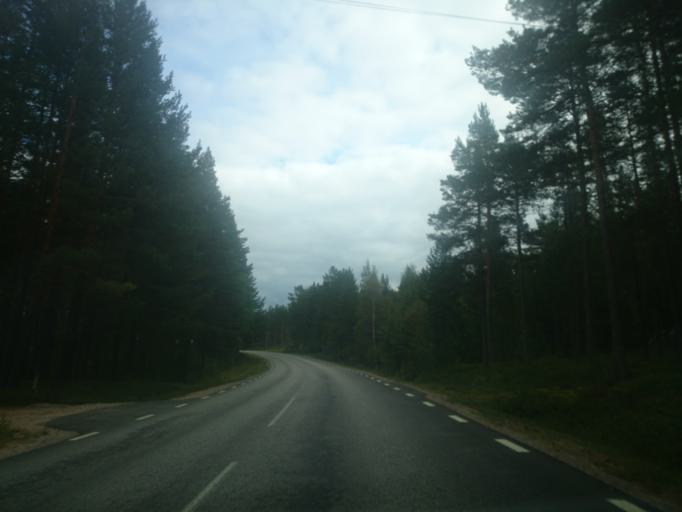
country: SE
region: Jaemtland
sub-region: Harjedalens Kommun
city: Sveg
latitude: 62.0352
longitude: 14.7580
